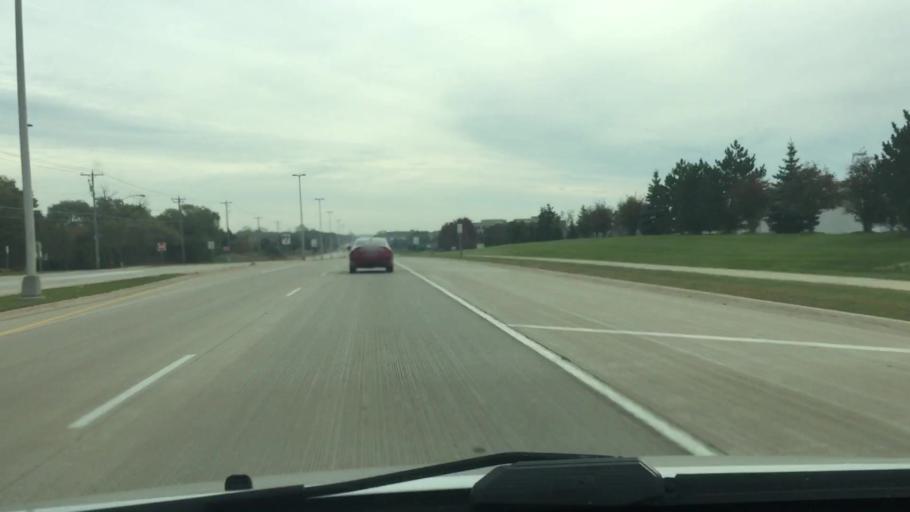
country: US
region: Wisconsin
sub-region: Milwaukee County
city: Franklin
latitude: 42.8725
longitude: -87.9756
